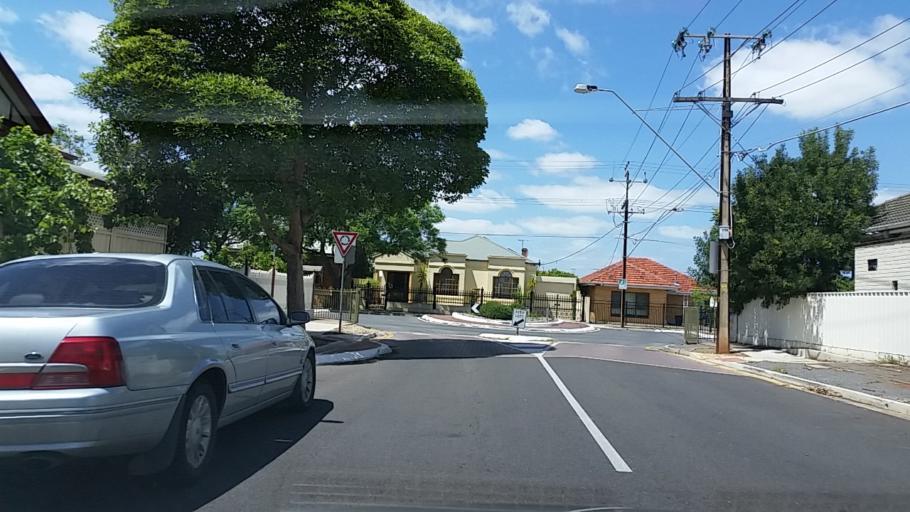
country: AU
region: South Australia
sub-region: City of West Torrens
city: Thebarton
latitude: -34.9290
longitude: 138.5588
